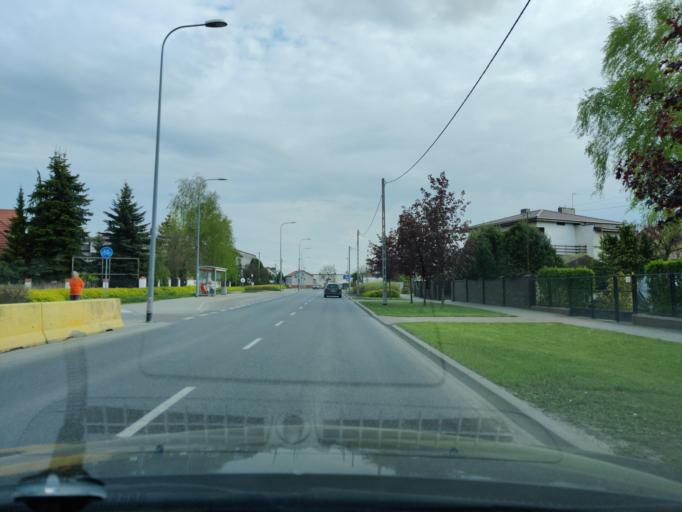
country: PL
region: Masovian Voivodeship
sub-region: Warszawa
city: Kabaty
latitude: 52.1334
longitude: 21.1008
